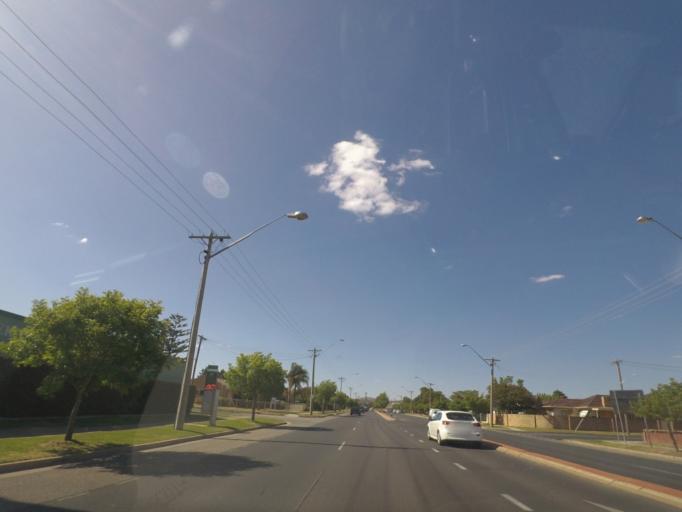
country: AU
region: New South Wales
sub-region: Albury Municipality
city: North Albury
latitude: -36.0569
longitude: 146.9327
